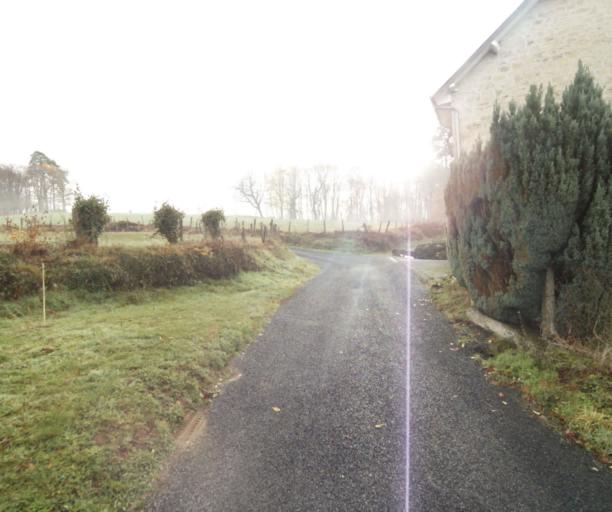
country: FR
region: Limousin
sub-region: Departement de la Correze
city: Cornil
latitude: 45.2025
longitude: 1.7110
